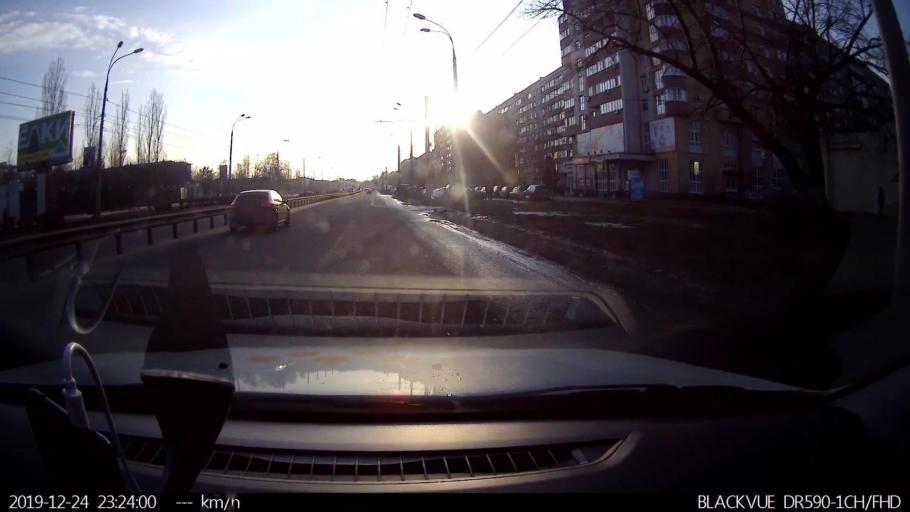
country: RU
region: Nizjnij Novgorod
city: Gorbatovka
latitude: 56.2554
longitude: 43.8538
